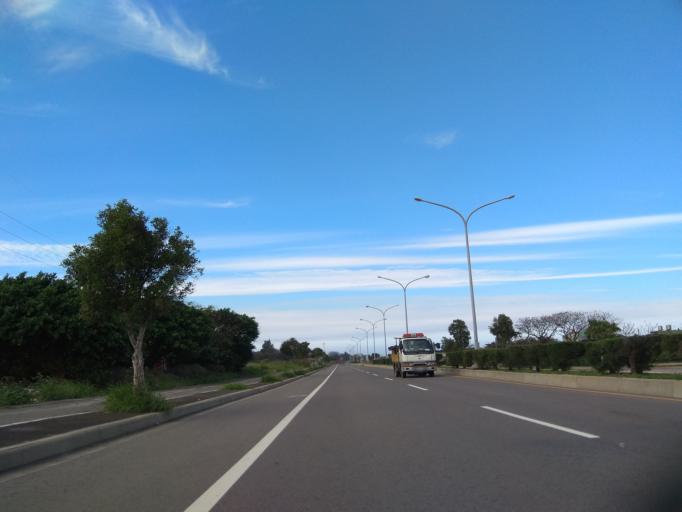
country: TW
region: Taiwan
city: Taoyuan City
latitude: 25.0656
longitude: 121.1756
